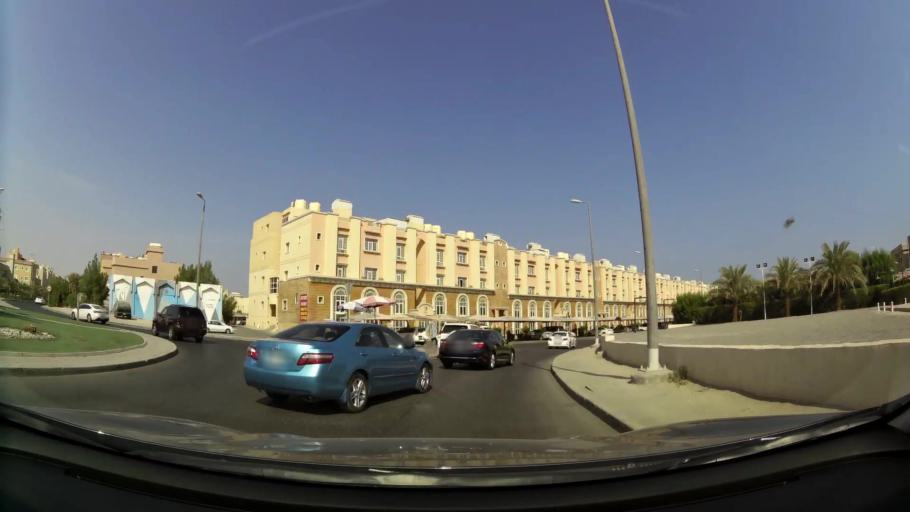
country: KW
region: Al Ahmadi
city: Al Manqaf
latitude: 29.1114
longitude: 48.1234
